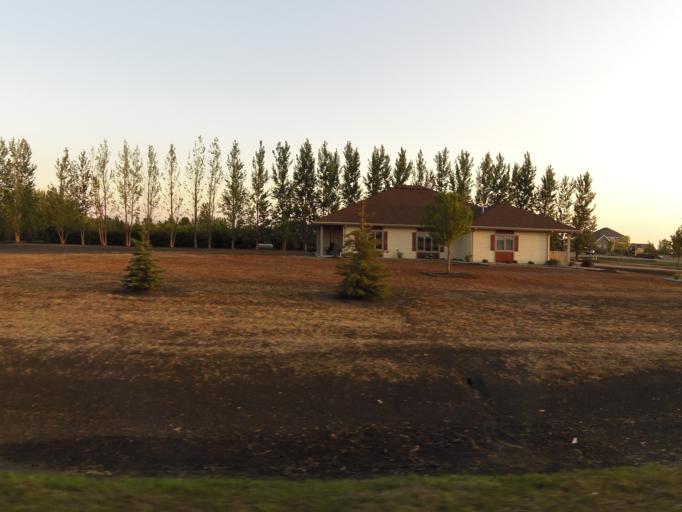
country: US
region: North Dakota
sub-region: Grand Forks County
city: Grand Forks
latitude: 47.8603
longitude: -97.0168
